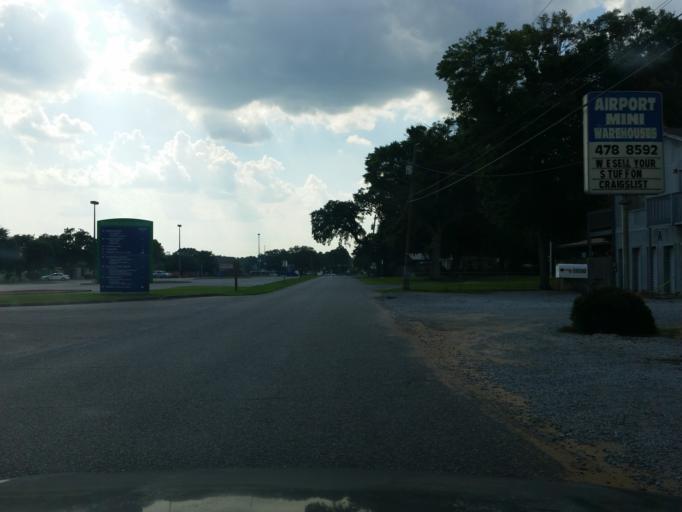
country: US
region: Florida
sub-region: Escambia County
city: Ferry Pass
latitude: 30.4822
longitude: -87.1983
